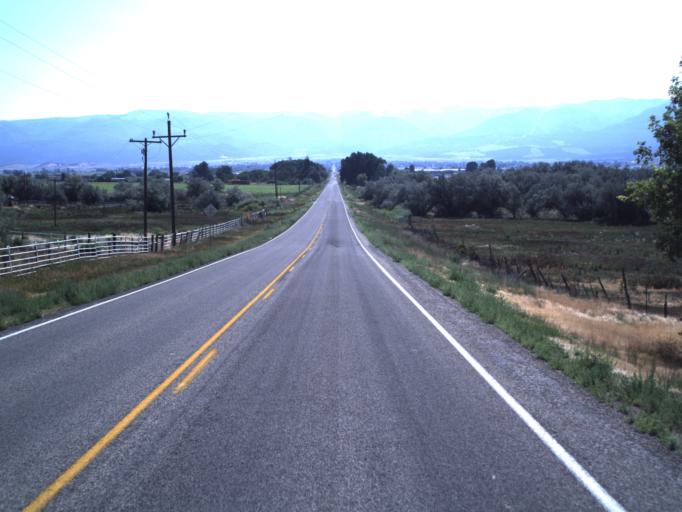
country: US
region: Utah
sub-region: Sanpete County
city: Mount Pleasant
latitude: 39.5467
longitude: -111.5223
